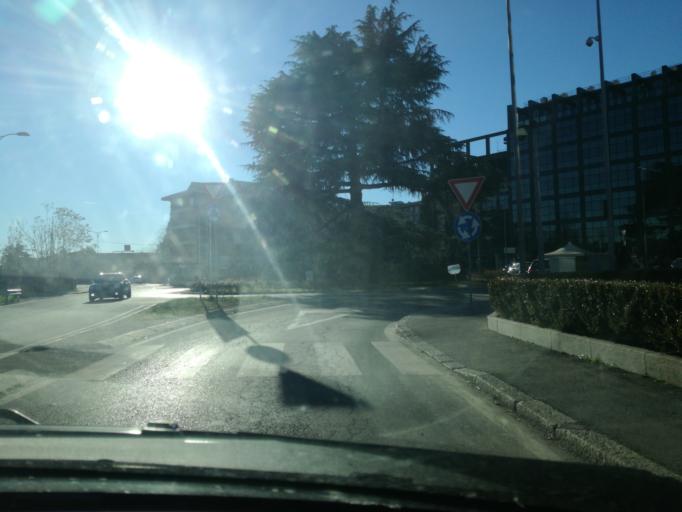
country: IT
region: Lombardy
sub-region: Provincia di Varese
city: Gallarate
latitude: 45.6668
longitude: 8.7962
